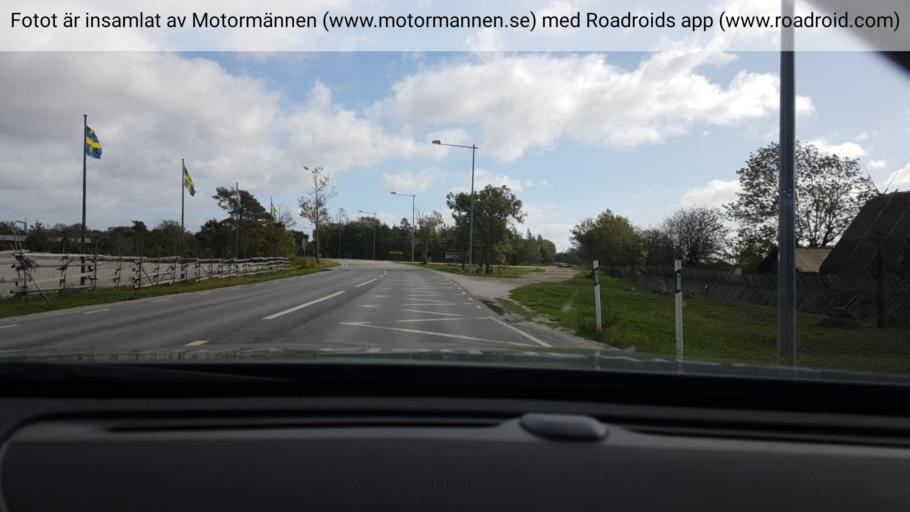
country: SE
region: Gotland
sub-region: Gotland
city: Slite
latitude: 57.8530
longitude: 19.0285
